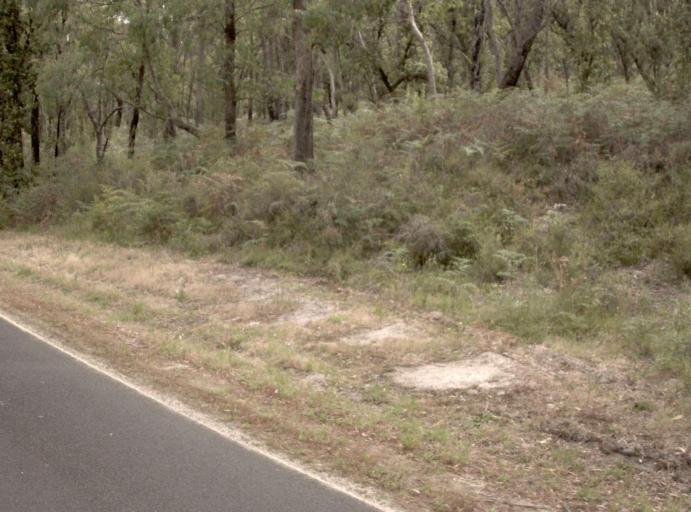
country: AU
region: Victoria
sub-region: Latrobe
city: Traralgon
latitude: -38.4164
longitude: 146.8164
